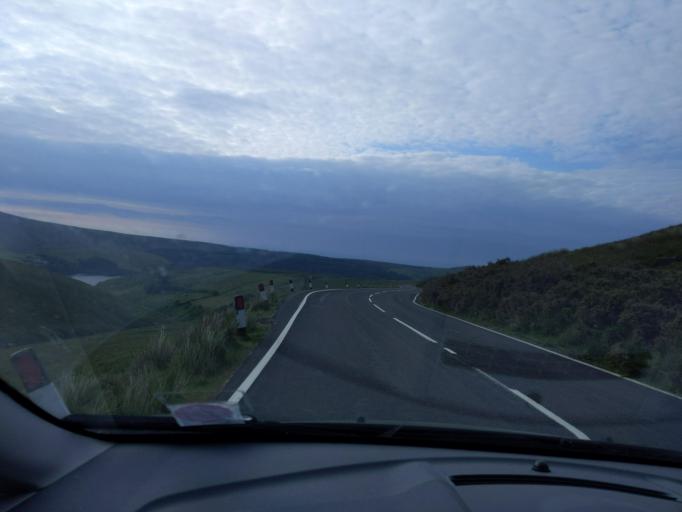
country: IM
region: Laxey
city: Laxey
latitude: 54.2572
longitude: -4.4755
